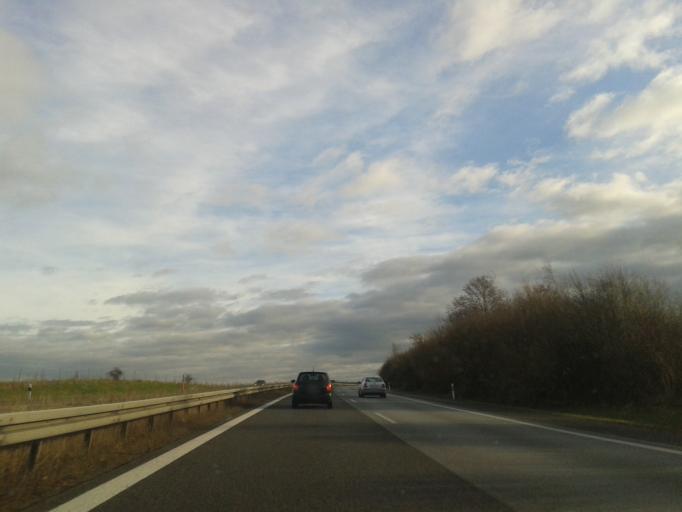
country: DE
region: Saxony
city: Goda
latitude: 51.2032
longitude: 14.3116
